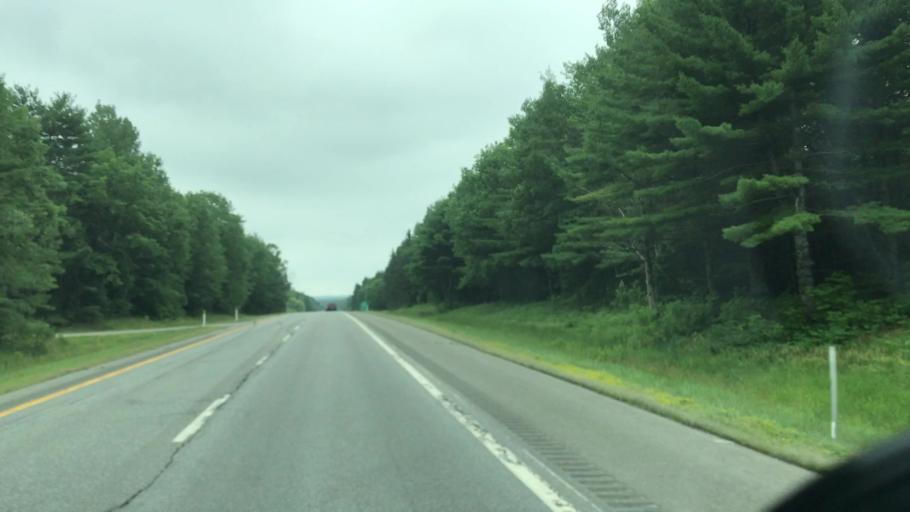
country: US
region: Maine
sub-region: Penobscot County
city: Milford
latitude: 44.9683
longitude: -68.7065
